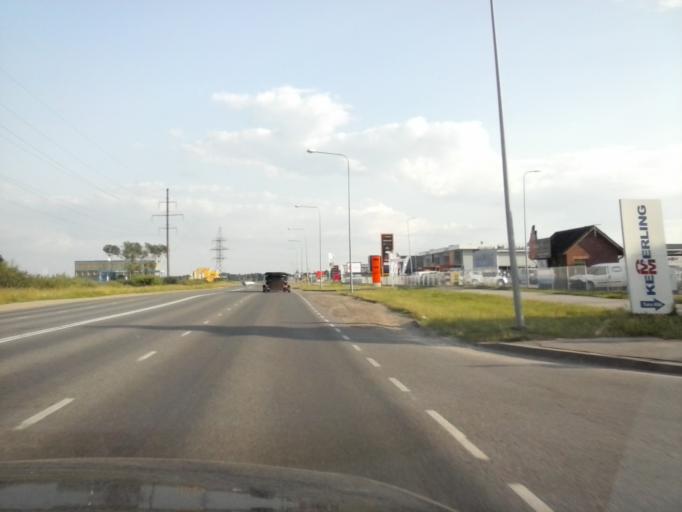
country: EE
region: Tartu
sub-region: UElenurme vald
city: Ulenurme
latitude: 58.3482
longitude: 26.7409
